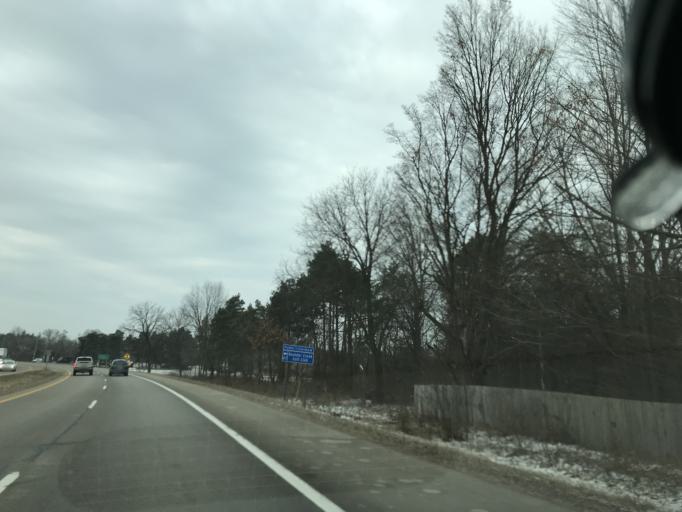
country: US
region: Michigan
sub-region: Kent County
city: Northview
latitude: 43.0736
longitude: -85.5770
